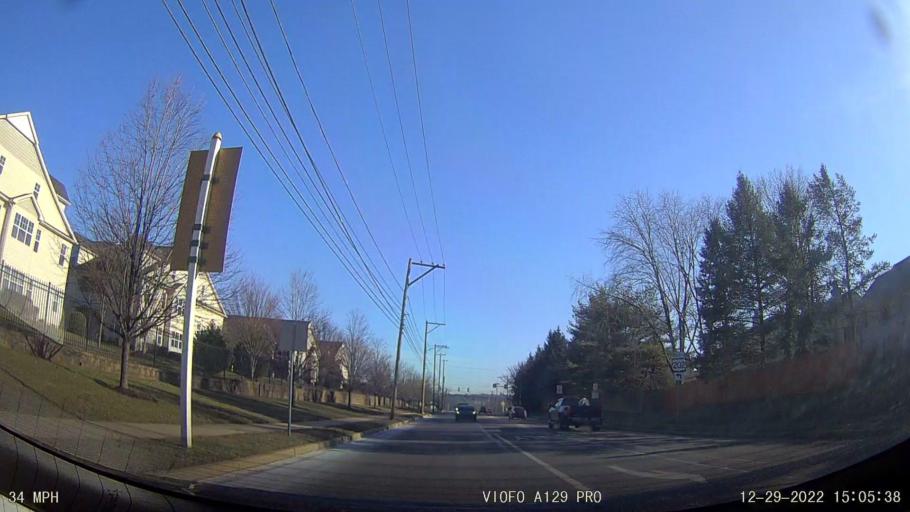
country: US
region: Pennsylvania
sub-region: Montgomery County
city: Norristown
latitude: 40.1307
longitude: -75.3263
